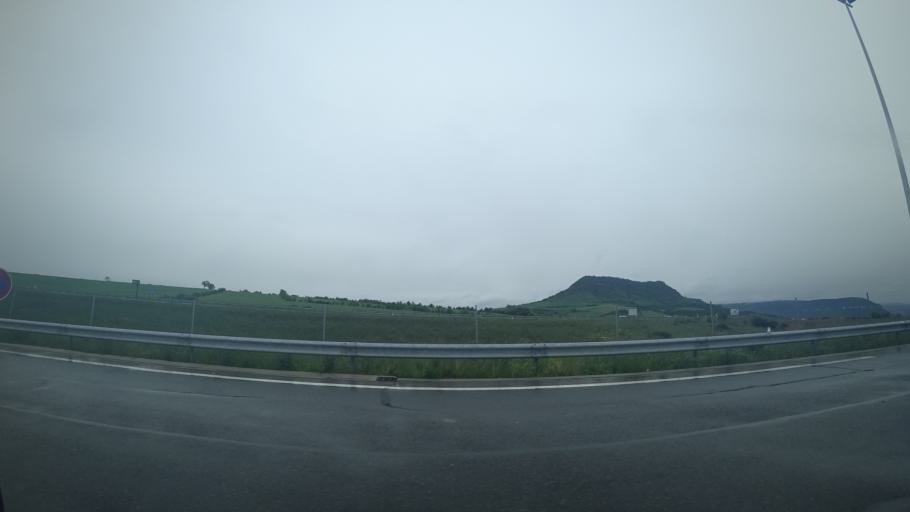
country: FR
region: Midi-Pyrenees
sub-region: Departement de l'Aveyron
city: Creissels
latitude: 44.1334
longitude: 3.0270
